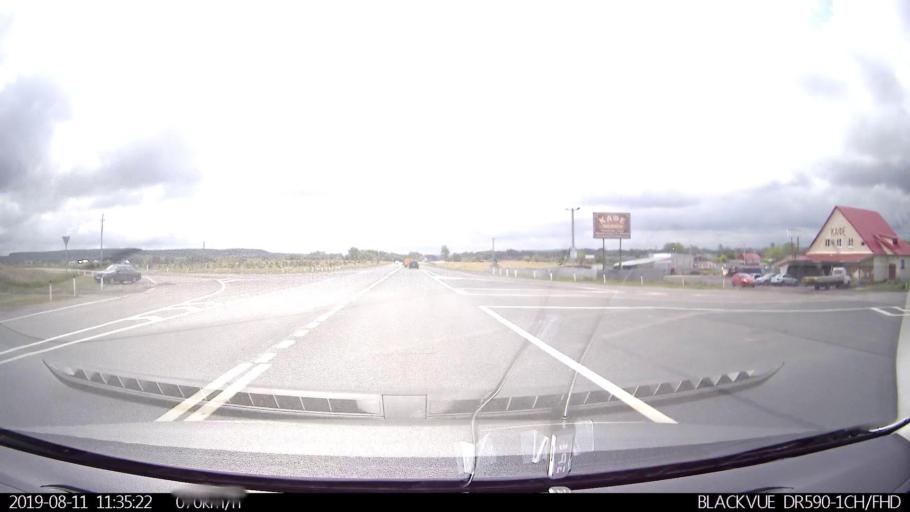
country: RU
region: Ulyanovsk
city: Silikatnyy
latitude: 54.0072
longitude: 48.2191
